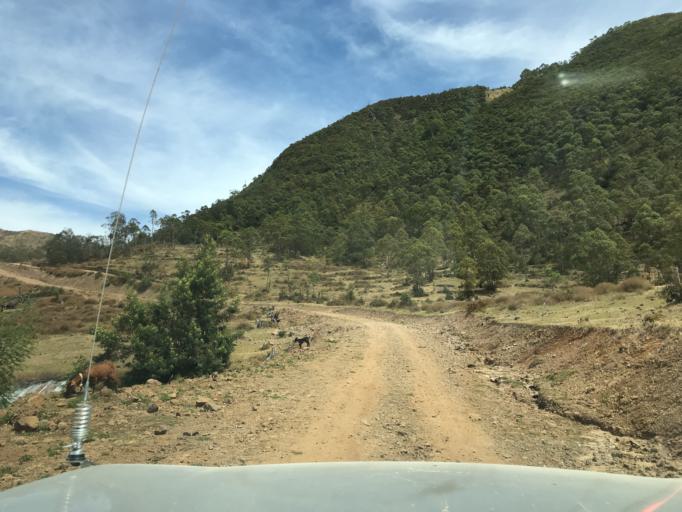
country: TL
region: Ainaro
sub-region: Ainaro
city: Ainaro
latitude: -8.8763
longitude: 125.5308
